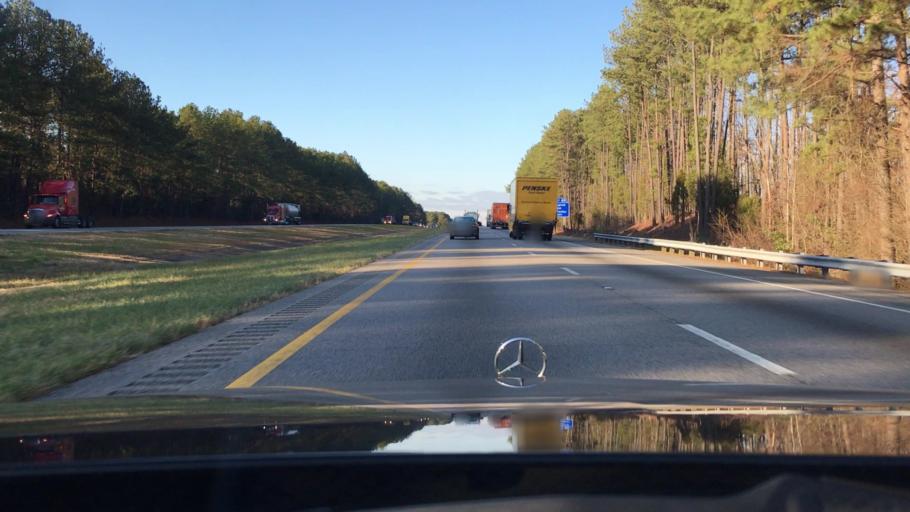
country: US
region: South Carolina
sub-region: Chester County
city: Eureka Mill
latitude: 34.7360
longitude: -81.0345
